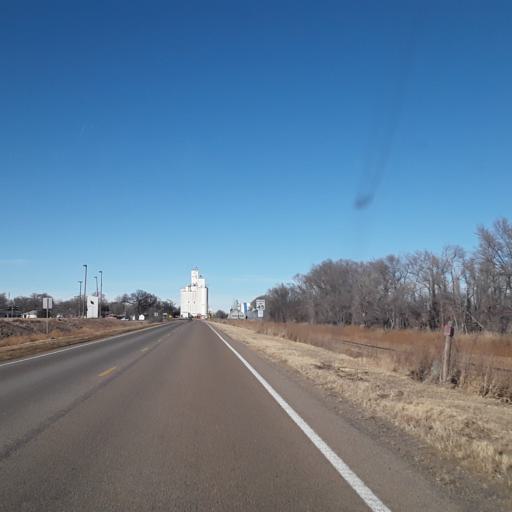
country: US
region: Nebraska
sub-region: Frontier County
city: Stockville
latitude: 40.6530
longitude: -100.6156
